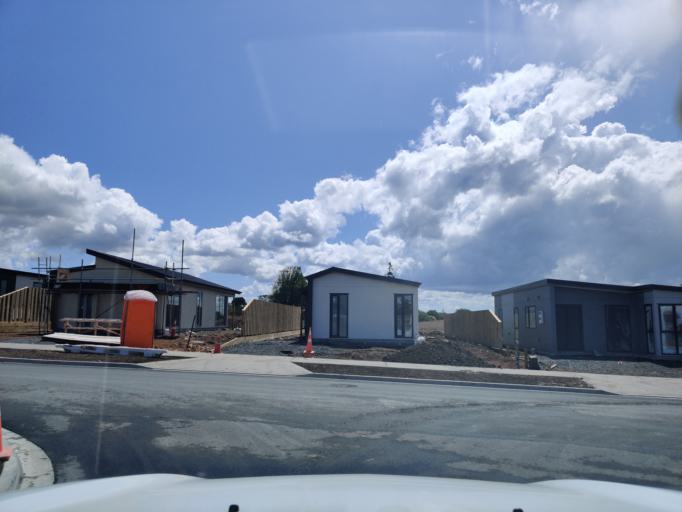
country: NZ
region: Waikato
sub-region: Waikato District
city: Te Kauwhata
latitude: -37.4135
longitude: 175.1497
